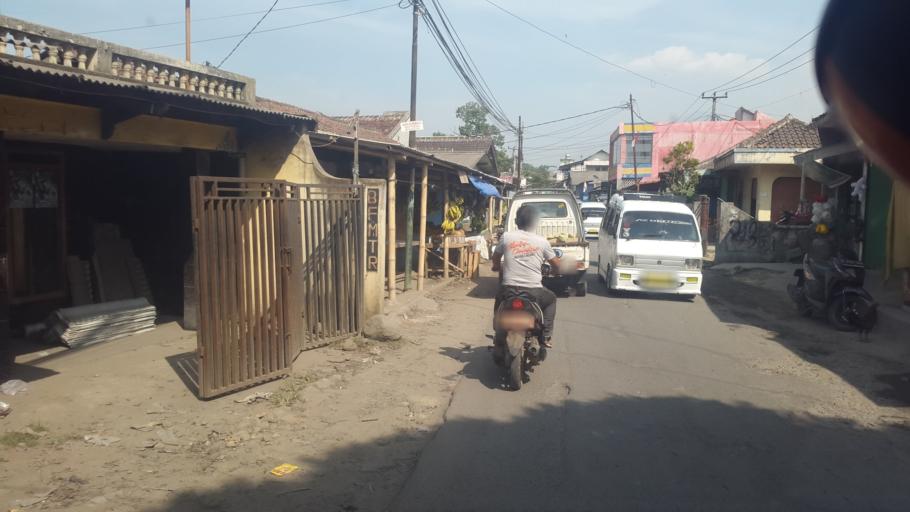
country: ID
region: West Java
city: Cicurug
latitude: -6.7990
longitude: 106.7565
